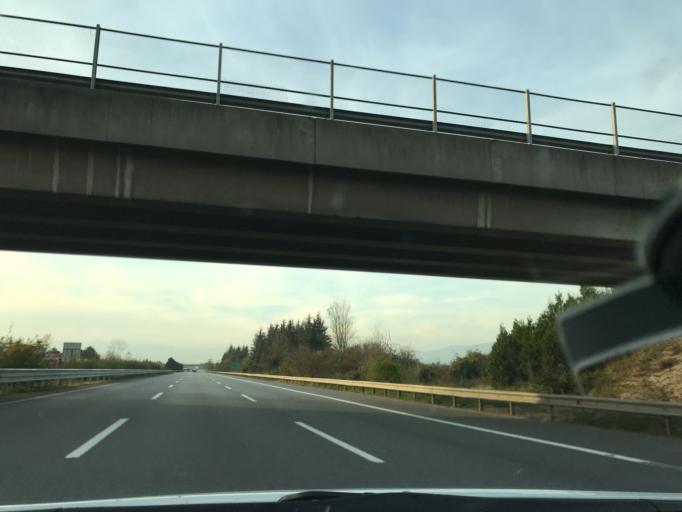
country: TR
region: Duzce
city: Cilimli
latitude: 40.8374
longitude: 31.0313
